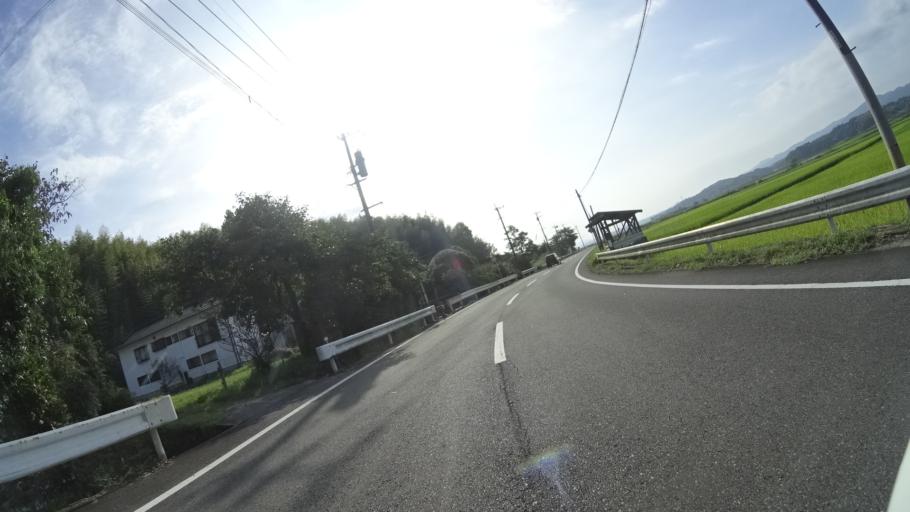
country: JP
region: Kagoshima
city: Okuchi-shinohara
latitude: 32.0243
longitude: 130.6055
